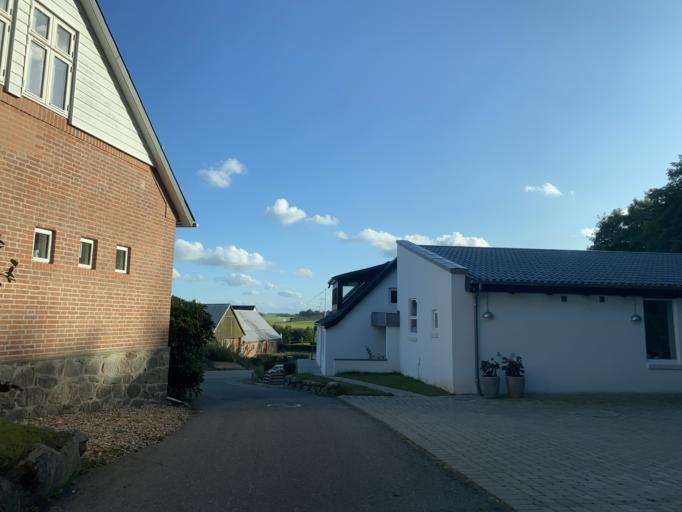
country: DK
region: Central Jutland
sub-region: Skanderborg Kommune
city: Ry
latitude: 56.1509
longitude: 9.7821
